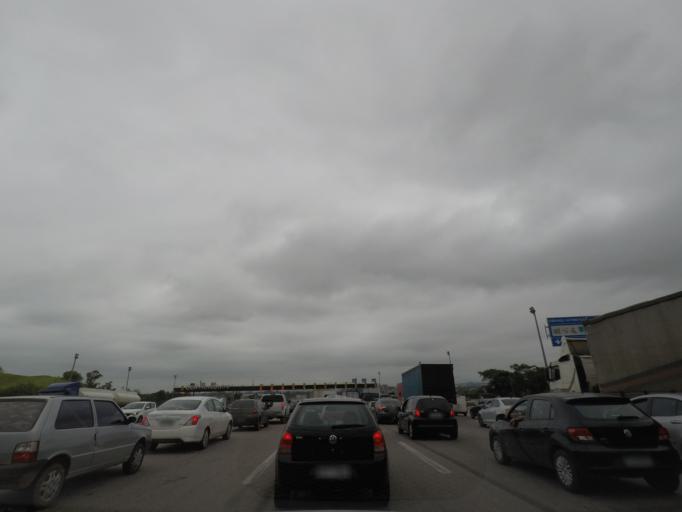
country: BR
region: Sao Paulo
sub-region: Jacarei
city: Jacarei
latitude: -23.2974
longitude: -46.0088
